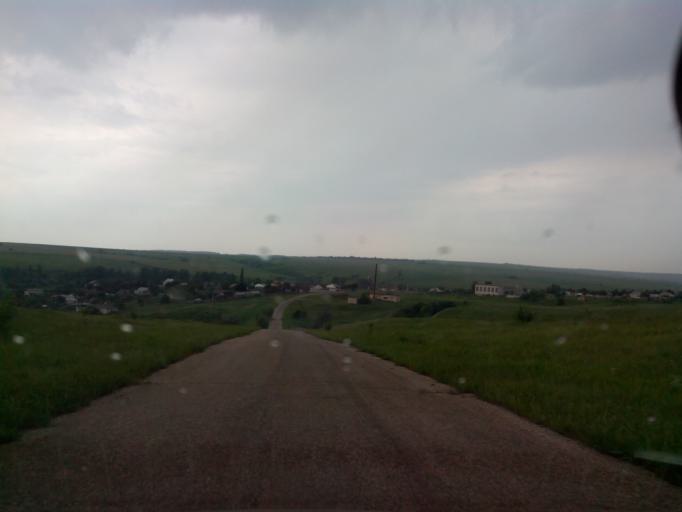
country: RU
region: Volgograd
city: Slashchevskaya
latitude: 49.7813
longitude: 42.4469
